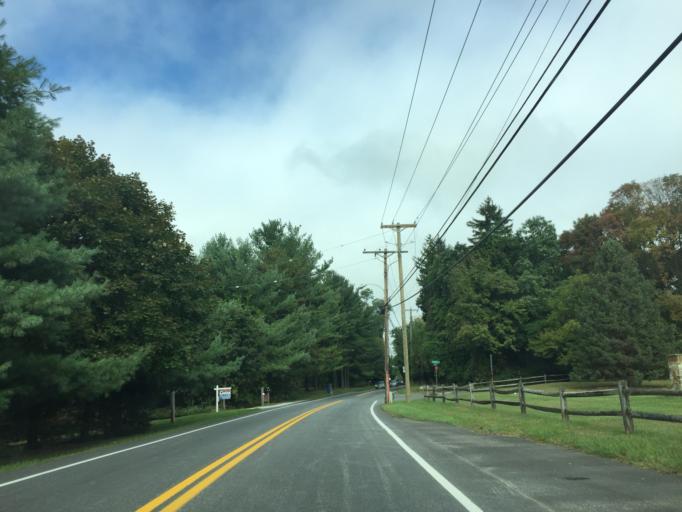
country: US
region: Maryland
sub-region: Baltimore County
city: Garrison
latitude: 39.4410
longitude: -76.7144
